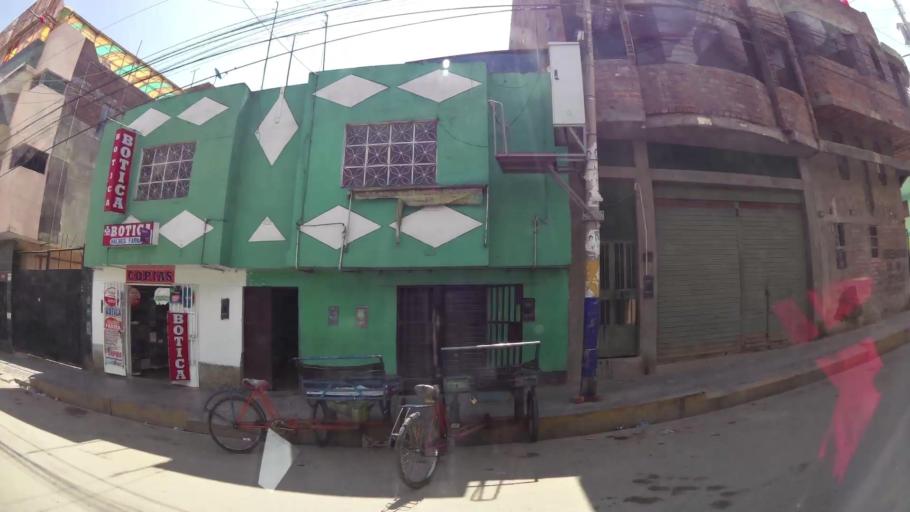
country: PE
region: Junin
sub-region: Provincia de Huancayo
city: Huancayo
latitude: -12.0687
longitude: -75.1999
